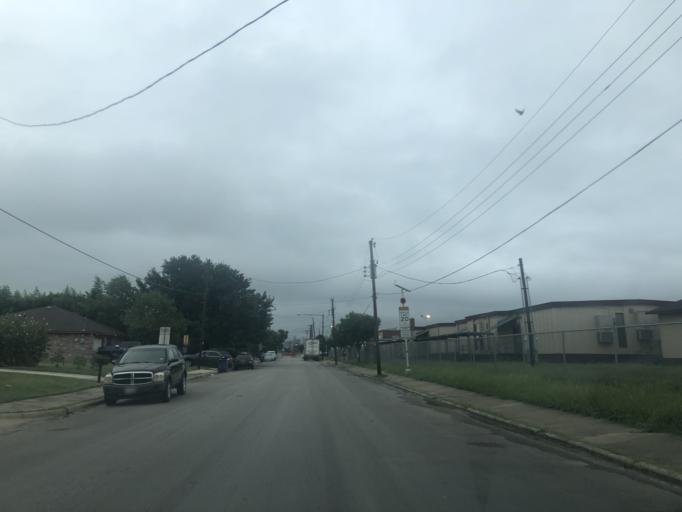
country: US
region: Texas
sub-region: Dallas County
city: Cockrell Hill
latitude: 32.7855
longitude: -96.8766
